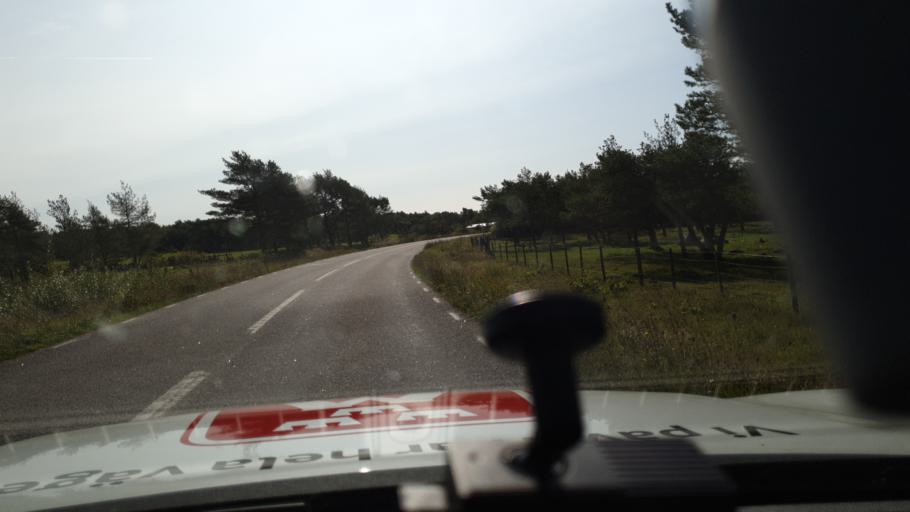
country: SE
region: Gotland
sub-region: Gotland
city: Hemse
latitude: 57.1018
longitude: 18.3022
